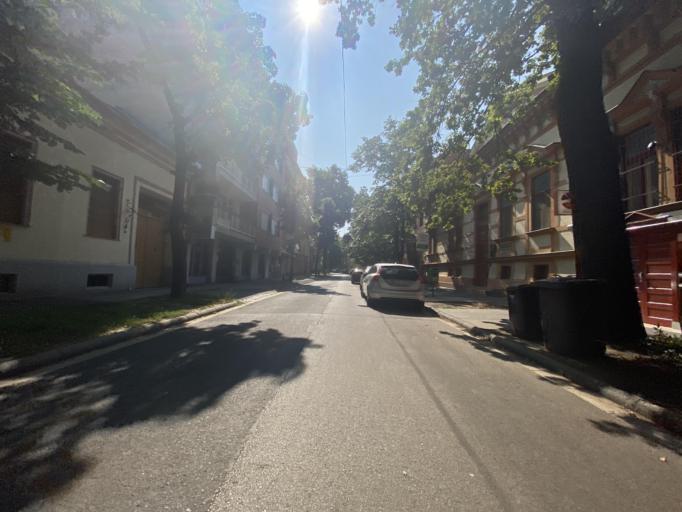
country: HU
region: Csongrad
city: Szeged
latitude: 46.2577
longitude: 20.1528
